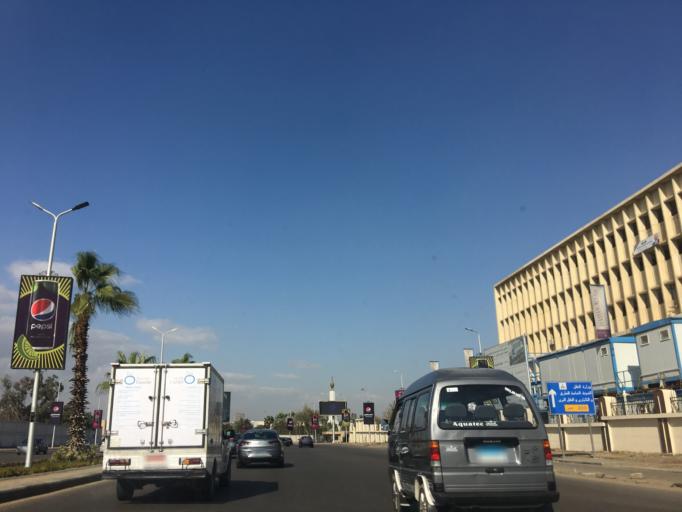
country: EG
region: Muhafazat al Qahirah
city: Cairo
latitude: 30.0538
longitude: 31.3075
